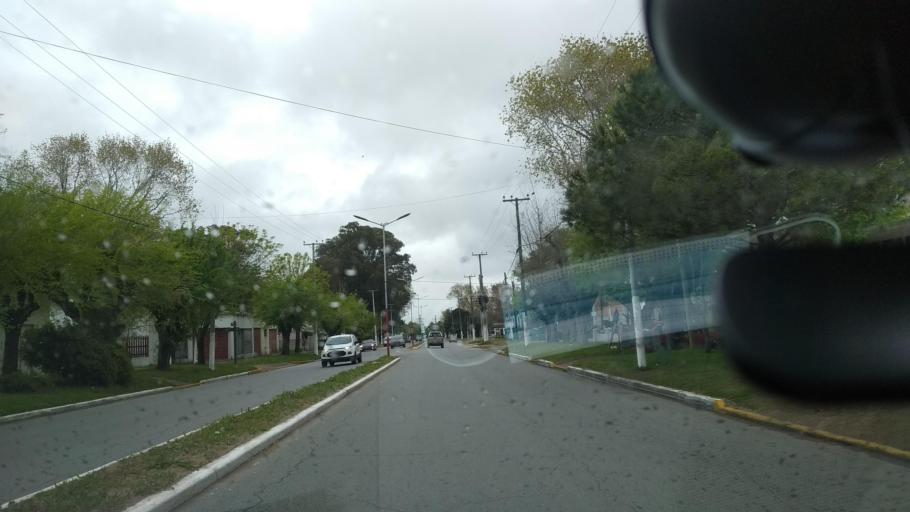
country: AR
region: Buenos Aires
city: San Clemente del Tuyu
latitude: -36.3768
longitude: -56.7197
